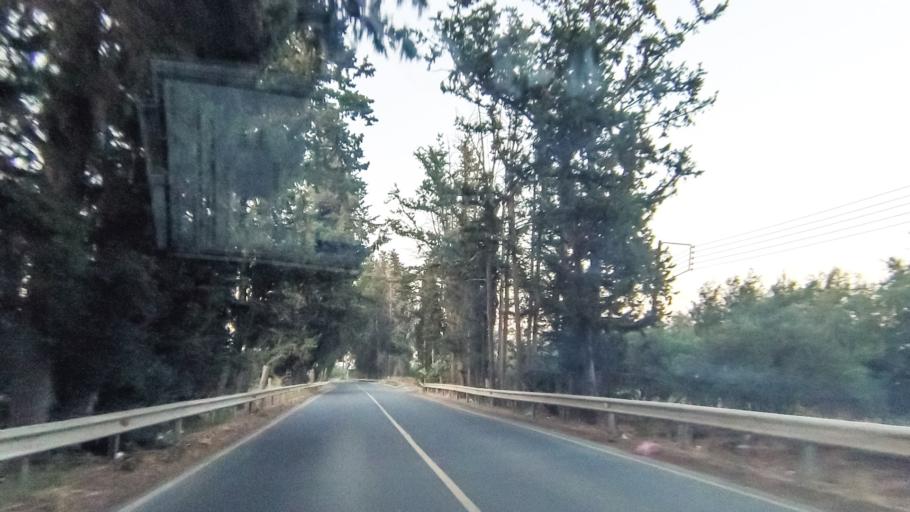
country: CY
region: Limassol
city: Ypsonas
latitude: 34.6537
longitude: 32.9917
